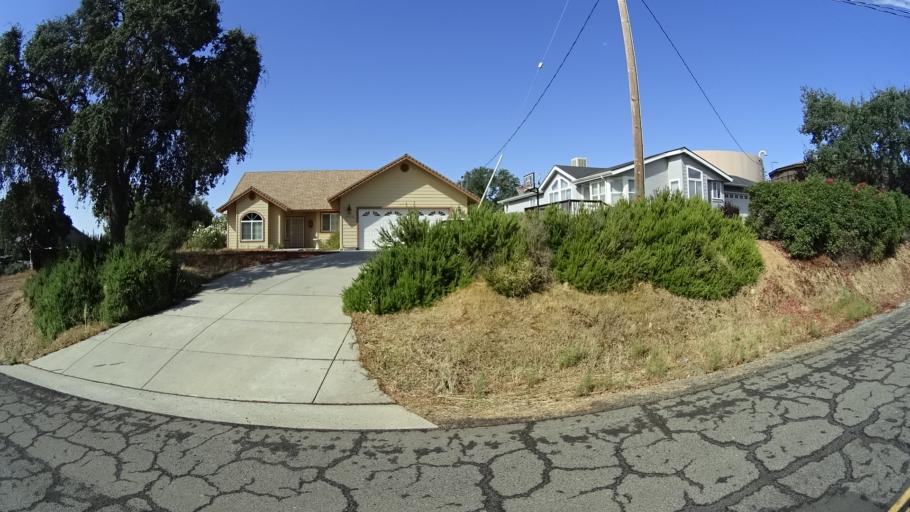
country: US
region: California
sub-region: Calaveras County
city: Copperopolis
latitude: 37.9122
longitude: -120.6125
